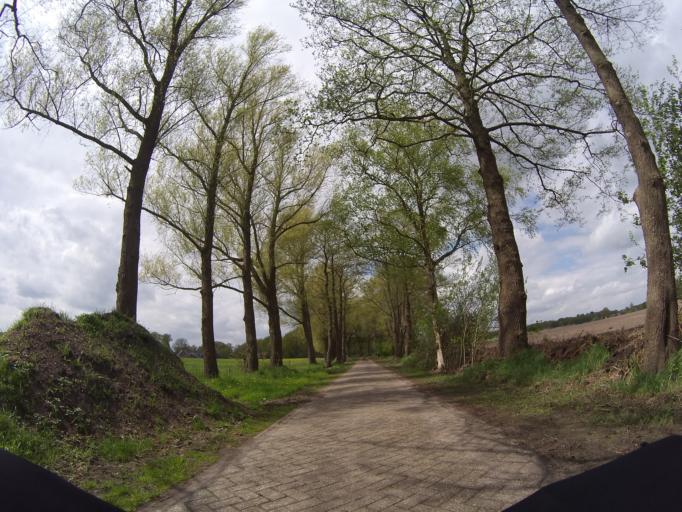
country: NL
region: Overijssel
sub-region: Gemeente Hardenberg
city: Hardenberg
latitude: 52.5466
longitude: 6.5883
